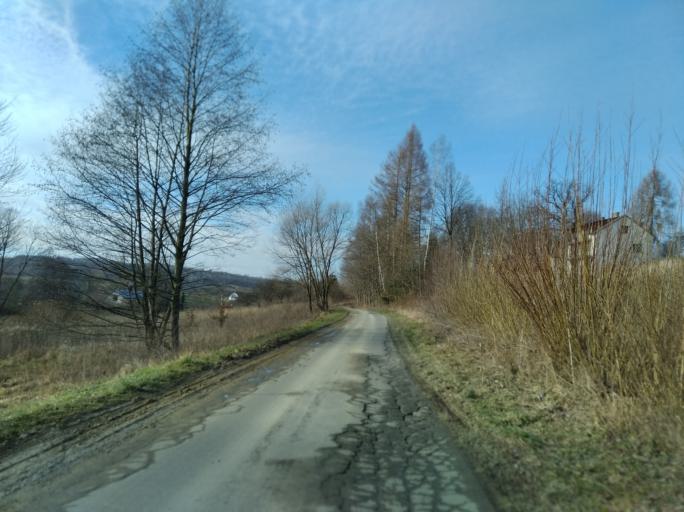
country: PL
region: Subcarpathian Voivodeship
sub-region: Powiat strzyzowski
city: Konieczkowa
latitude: 49.8307
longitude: 21.9373
